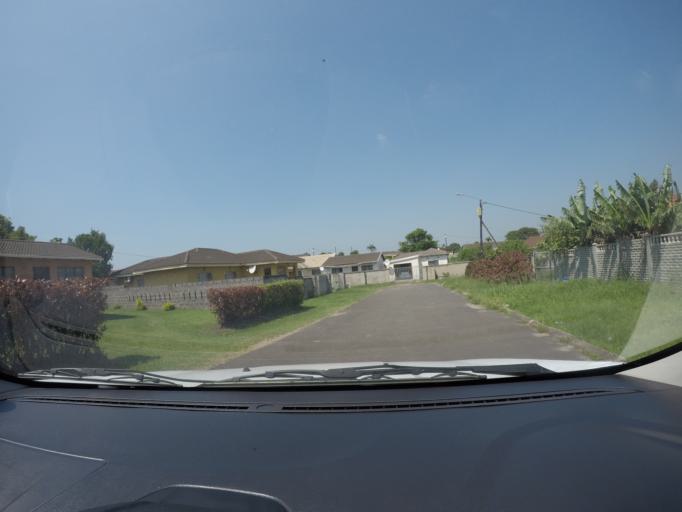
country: ZA
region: KwaZulu-Natal
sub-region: uThungulu District Municipality
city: eSikhawini
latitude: -28.8640
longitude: 31.9204
